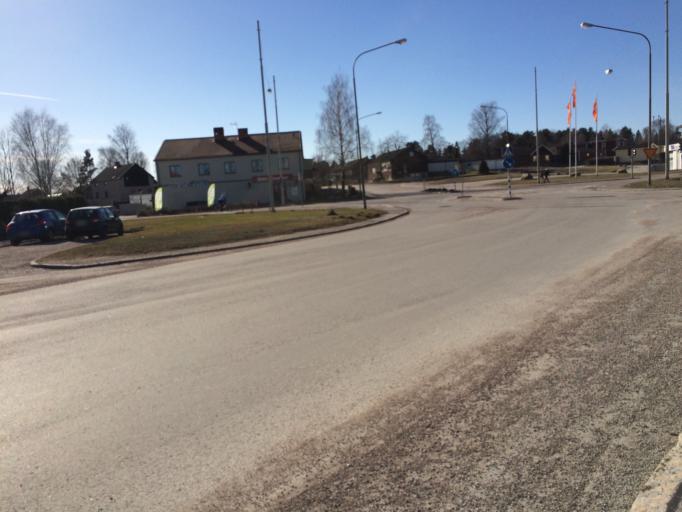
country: SE
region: Vaestmanland
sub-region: Hallstahammars Kommun
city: Hallstahammar
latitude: 59.6110
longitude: 16.2377
